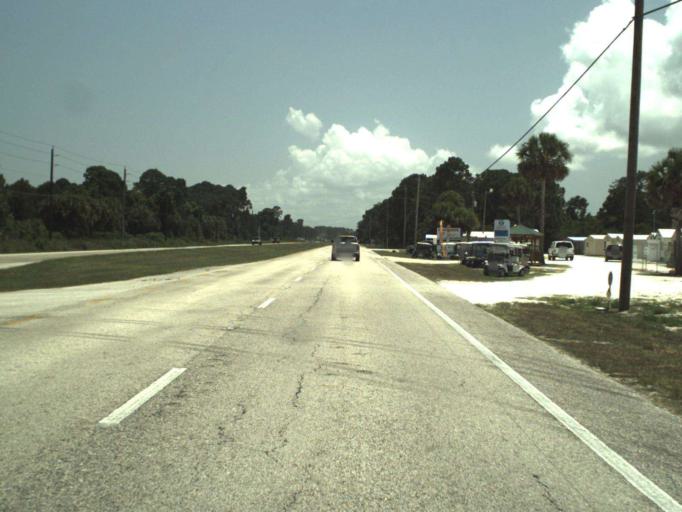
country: US
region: Florida
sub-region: Volusia County
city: Oak Hill
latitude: 28.8886
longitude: -80.8587
